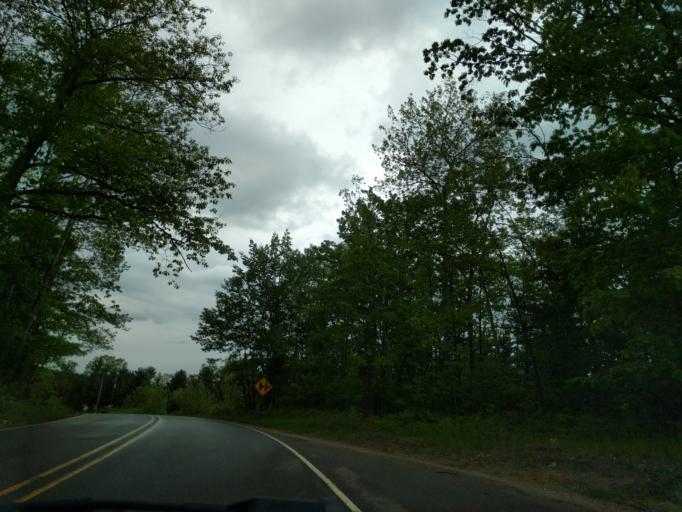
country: US
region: Michigan
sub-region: Marquette County
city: Trowbridge Park
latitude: 46.5769
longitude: -87.4708
